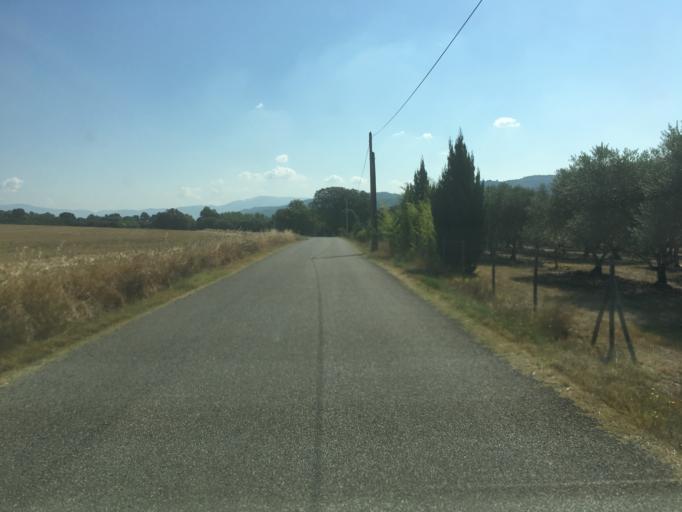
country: FR
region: Provence-Alpes-Cote d'Azur
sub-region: Departement des Alpes-de-Haute-Provence
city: Valensole
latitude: 43.8943
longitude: 5.9925
